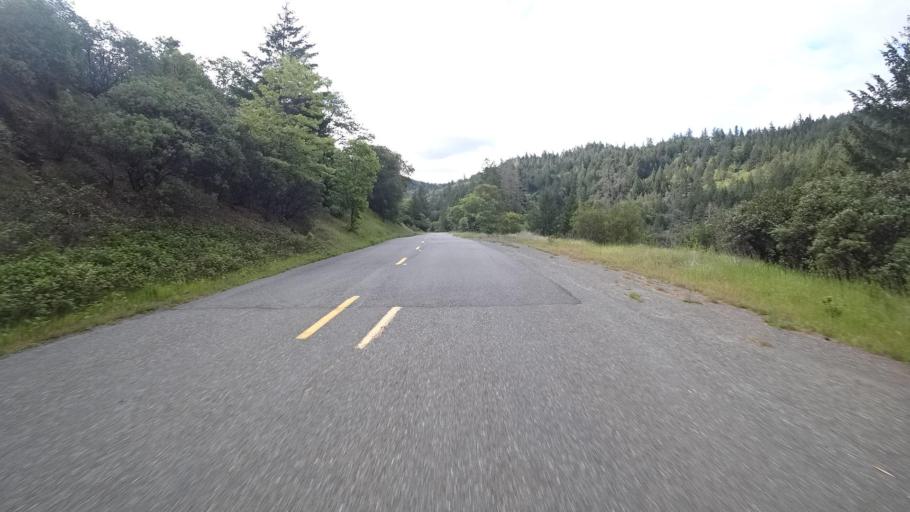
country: US
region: California
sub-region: Humboldt County
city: Redway
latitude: 40.1954
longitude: -123.5918
